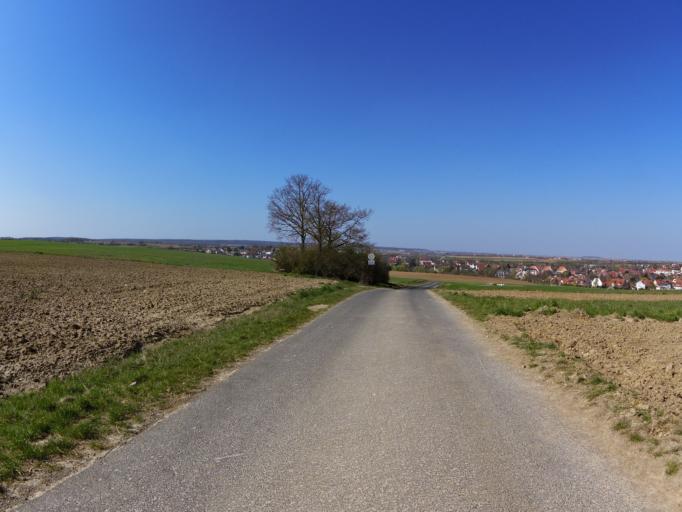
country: DE
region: Bavaria
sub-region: Regierungsbezirk Unterfranken
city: Kurnach
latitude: 49.8370
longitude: 10.0368
